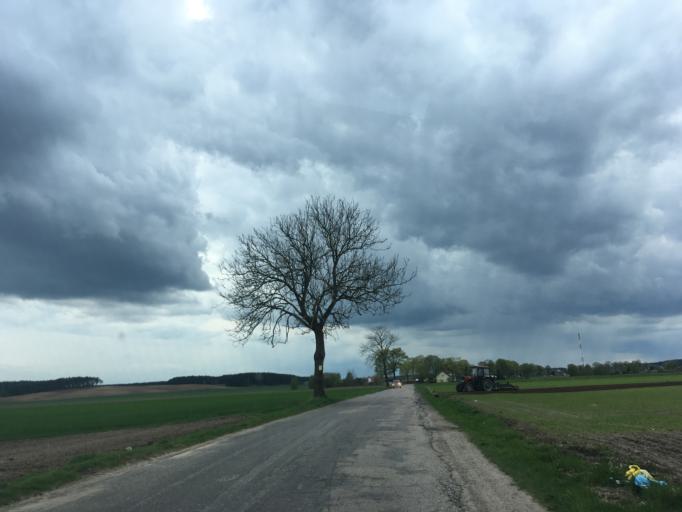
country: PL
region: Warmian-Masurian Voivodeship
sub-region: Powiat nidzicki
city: Kozlowo
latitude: 53.4080
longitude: 20.3260
